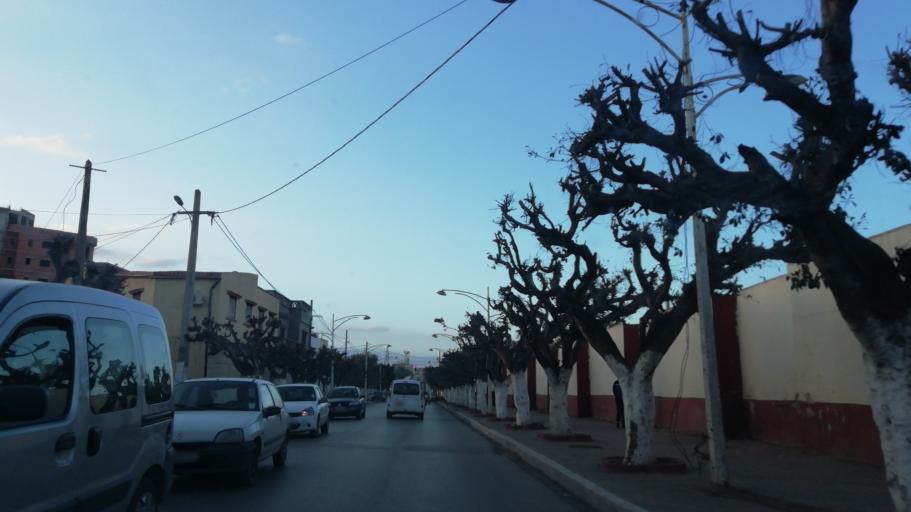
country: DZ
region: Oran
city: Oran
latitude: 35.6770
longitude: -0.6571
